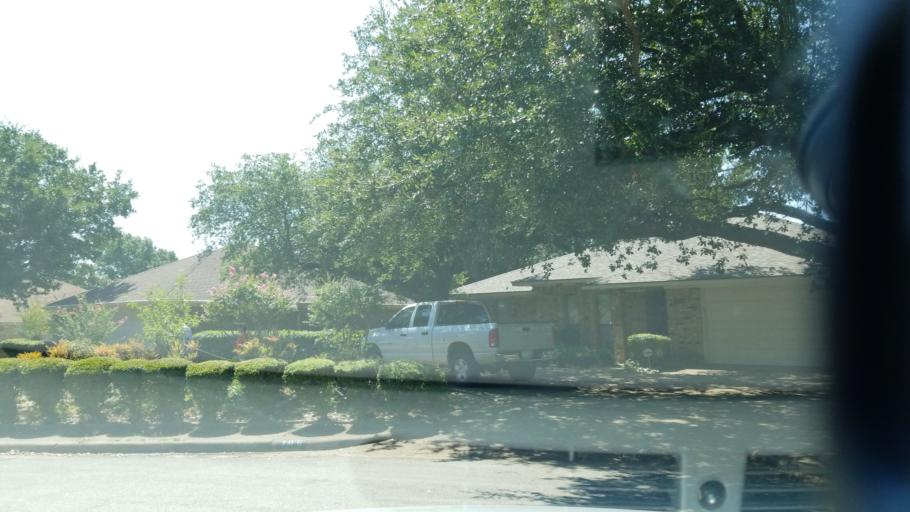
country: US
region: Texas
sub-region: Dallas County
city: Duncanville
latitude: 32.6429
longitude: -96.8955
